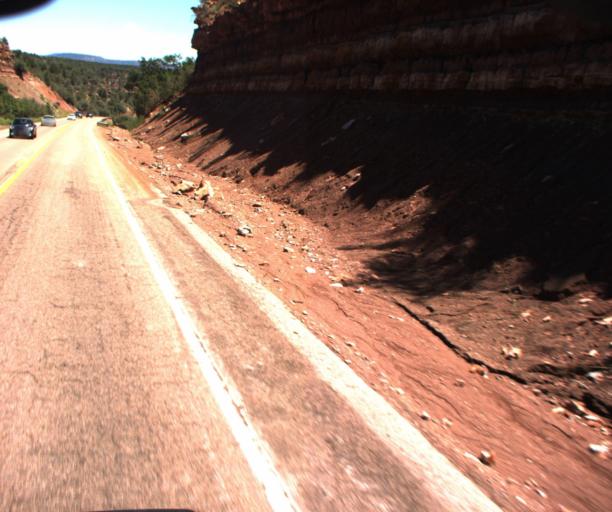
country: US
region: Arizona
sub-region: Navajo County
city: Cibecue
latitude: 33.9787
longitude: -110.3093
